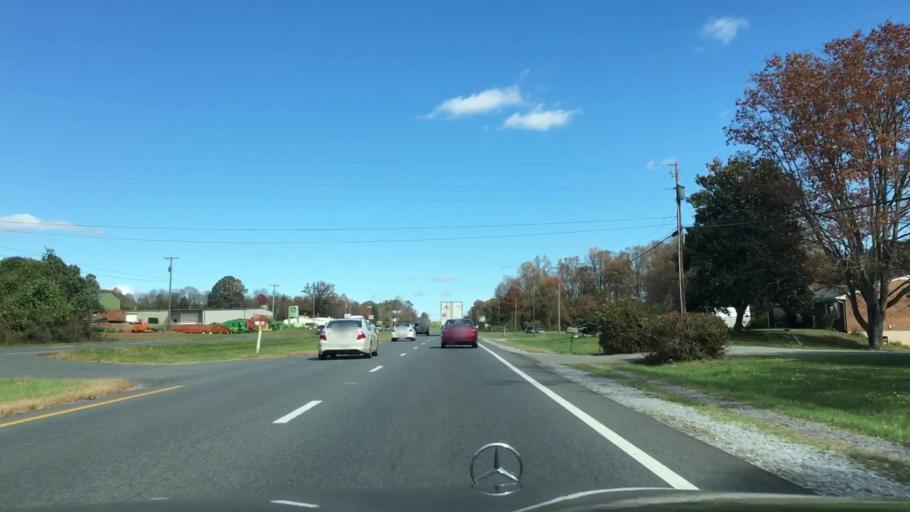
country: US
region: Virginia
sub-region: Campbell County
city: Rustburg
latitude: 37.2699
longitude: -79.1751
